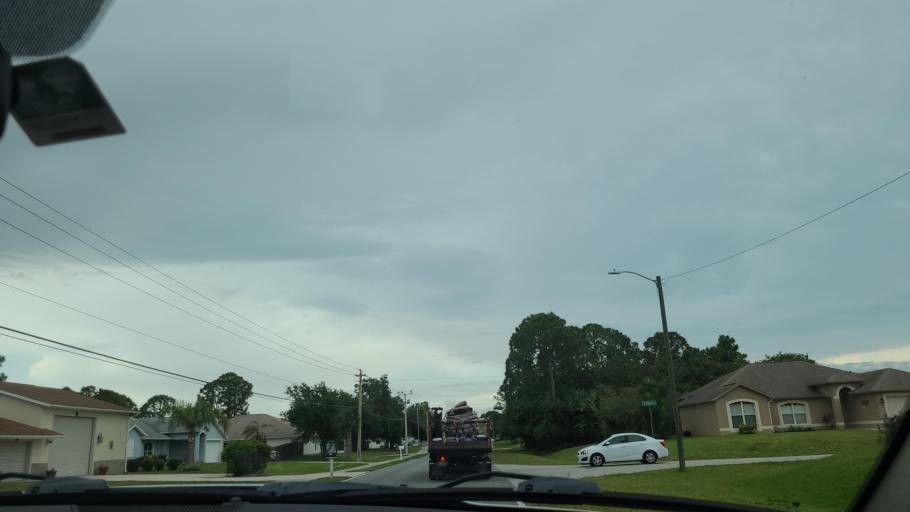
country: US
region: Florida
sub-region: Brevard County
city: West Melbourne
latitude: 28.0045
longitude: -80.6629
